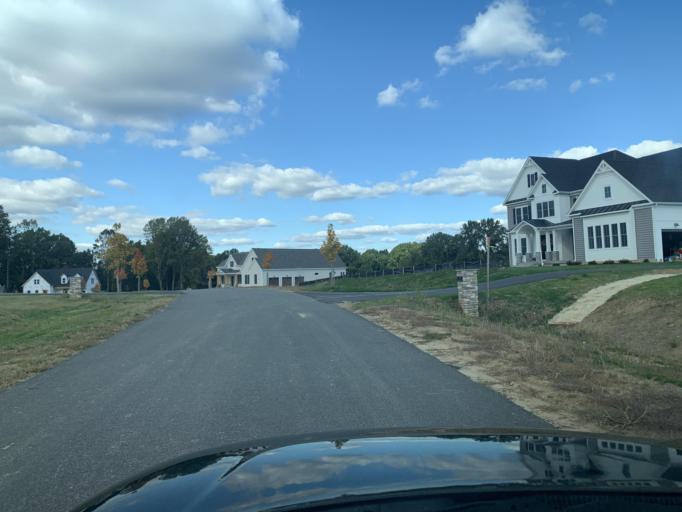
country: US
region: Maryland
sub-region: Harford County
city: Bel Air North
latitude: 39.5856
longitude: -76.4103
